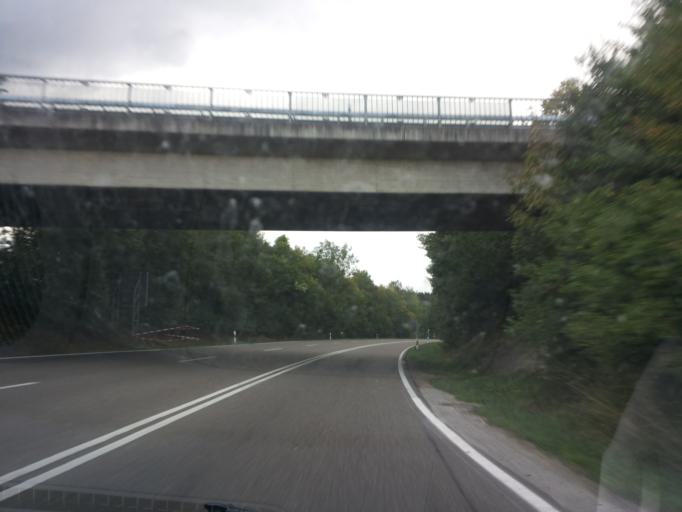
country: DE
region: Bavaria
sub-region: Upper Bavaria
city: Adelschlag
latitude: 48.8599
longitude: 11.2252
